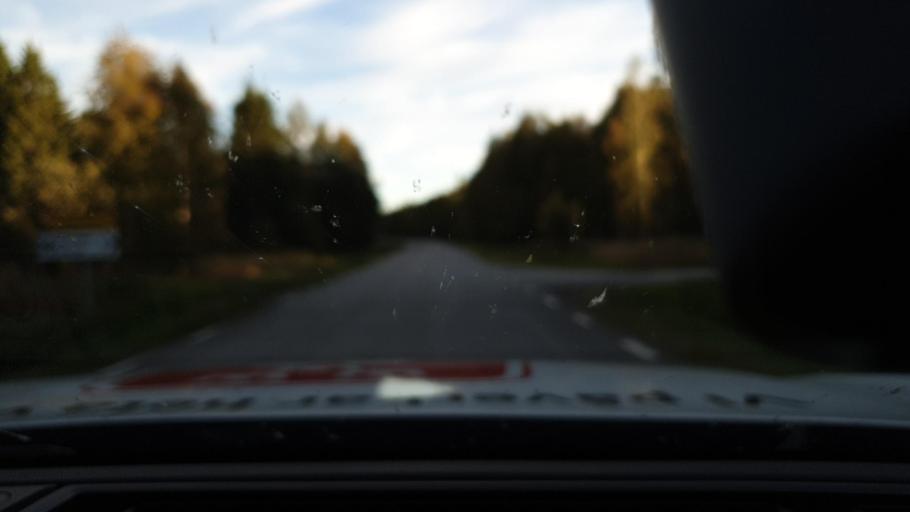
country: SE
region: Norrbotten
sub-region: Kalix Kommun
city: Toere
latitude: 65.8571
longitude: 22.6768
